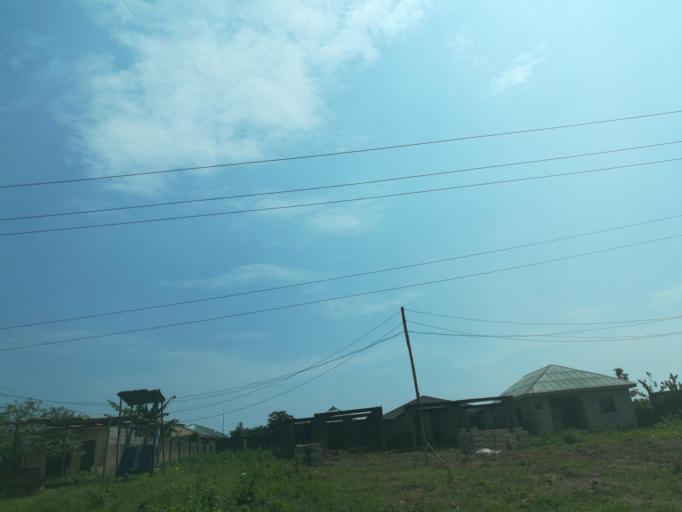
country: NG
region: Lagos
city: Ikorodu
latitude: 6.5950
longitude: 3.6352
